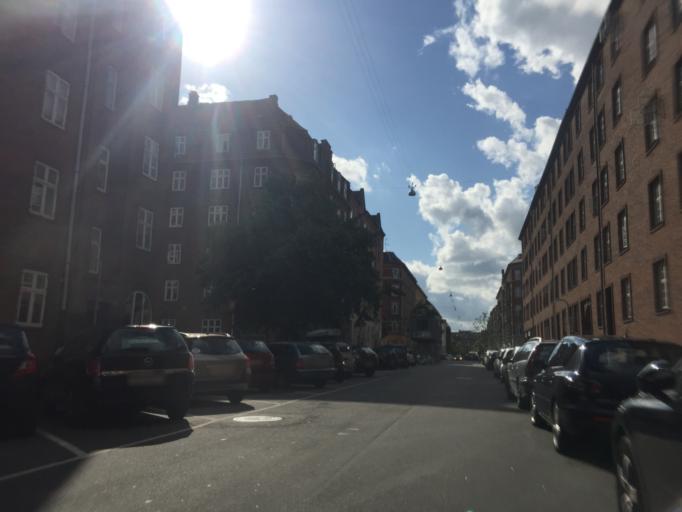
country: DK
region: Capital Region
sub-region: Frederiksberg Kommune
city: Frederiksberg
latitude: 55.6875
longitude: 12.5342
